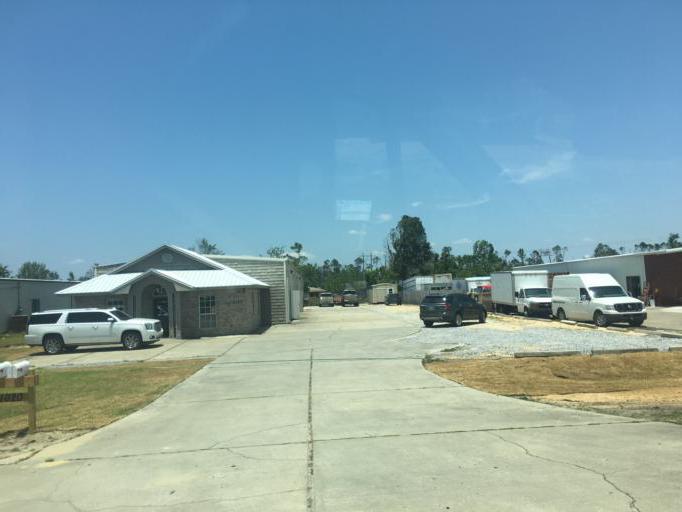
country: US
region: Florida
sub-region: Bay County
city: Lynn Haven
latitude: 30.2187
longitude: -85.6608
